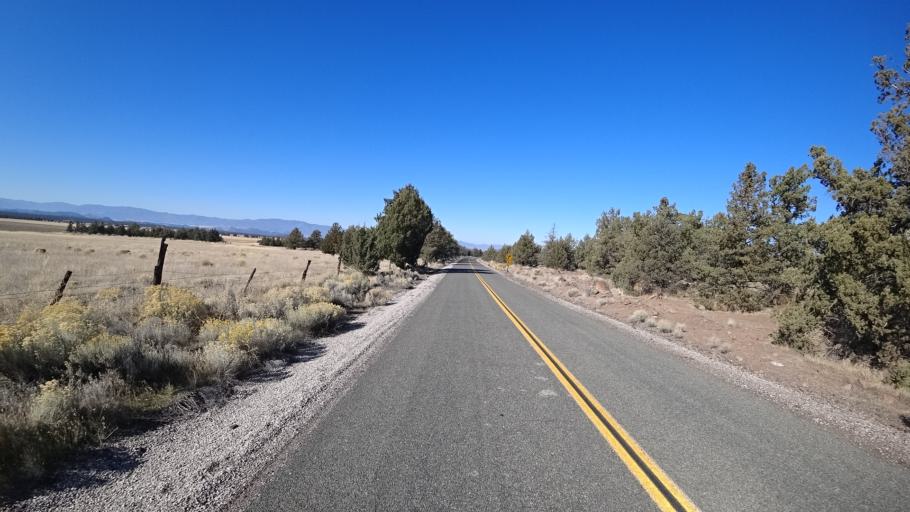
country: US
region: California
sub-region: Siskiyou County
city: Weed
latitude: 41.6020
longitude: -122.3031
